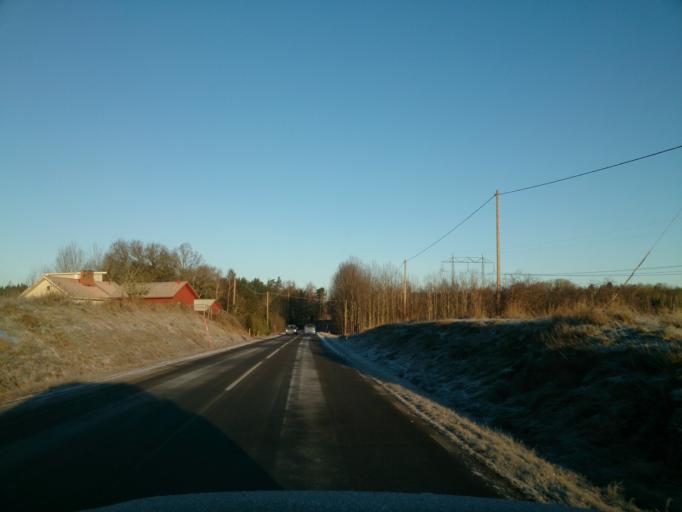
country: SE
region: OEstergoetland
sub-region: Atvidabergs Kommun
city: Atvidaberg
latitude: 58.3673
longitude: 16.0239
